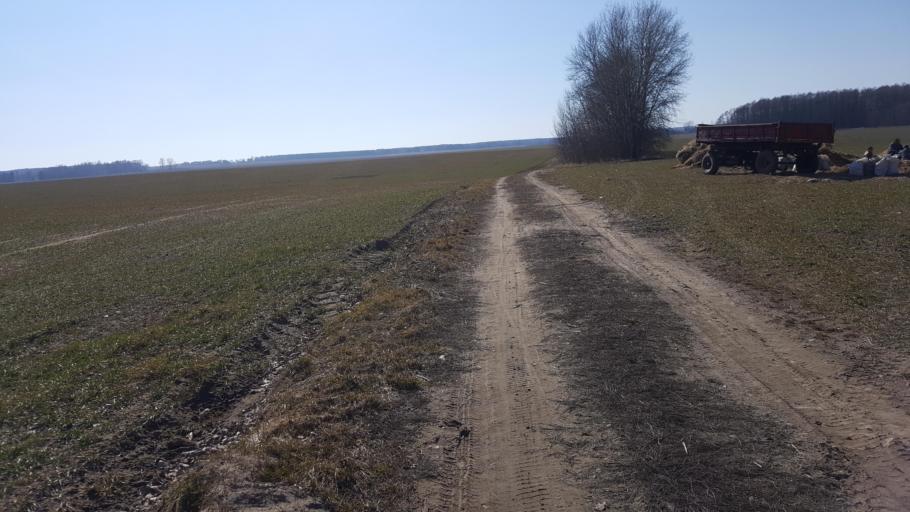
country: BY
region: Brest
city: Kamyanyets
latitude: 52.3696
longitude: 23.7756
